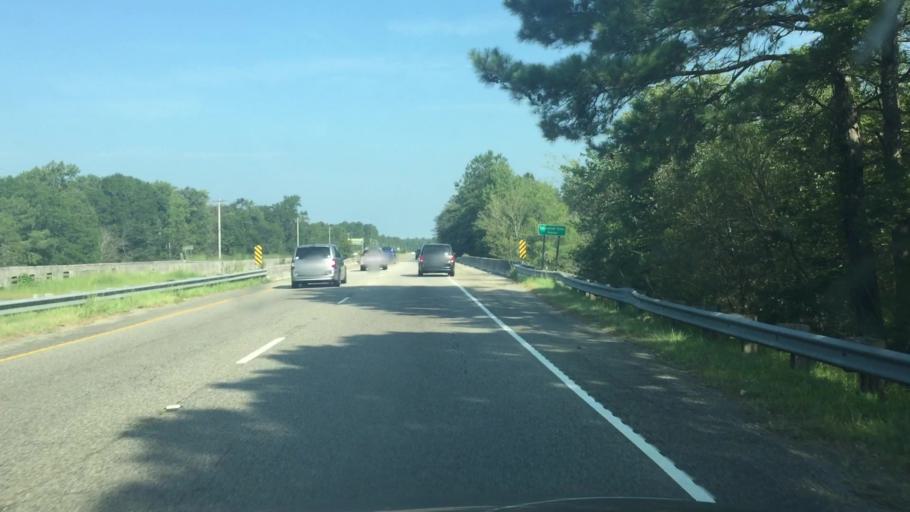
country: US
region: South Carolina
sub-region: Horry County
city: North Myrtle Beach
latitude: 33.9087
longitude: -78.7095
